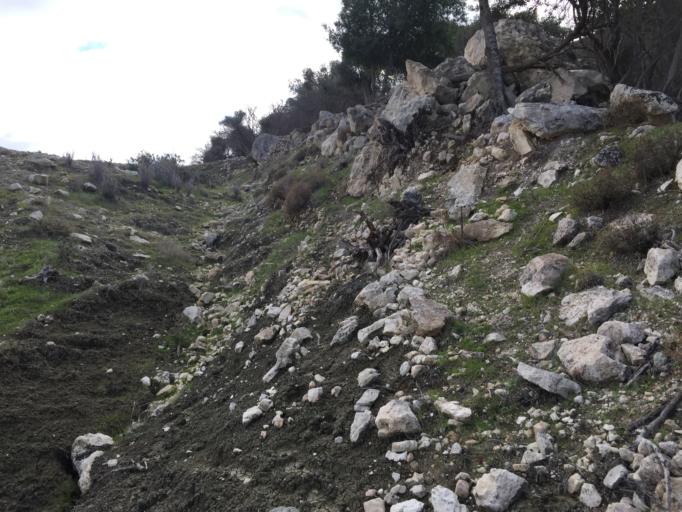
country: CY
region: Pafos
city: Pegeia
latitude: 34.9238
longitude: 32.3647
